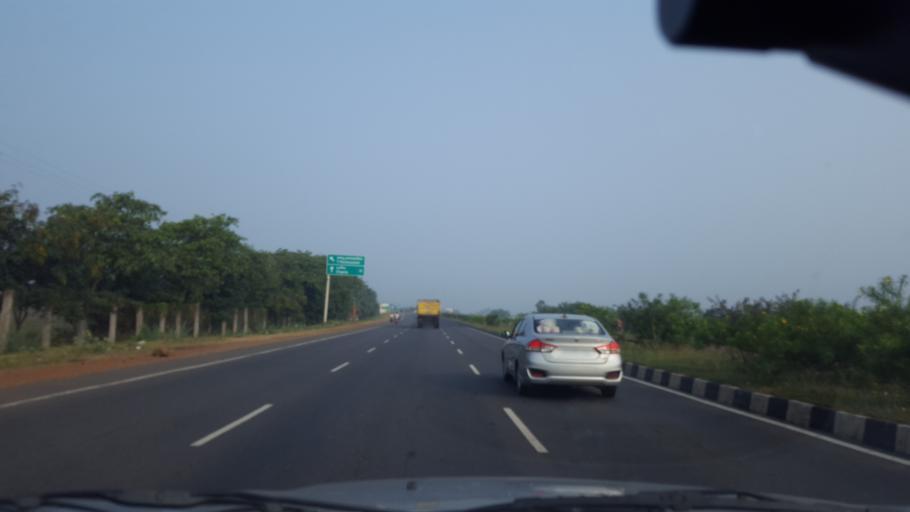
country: IN
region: Andhra Pradesh
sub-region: Prakasam
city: Ongole
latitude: 15.3838
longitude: 80.0403
